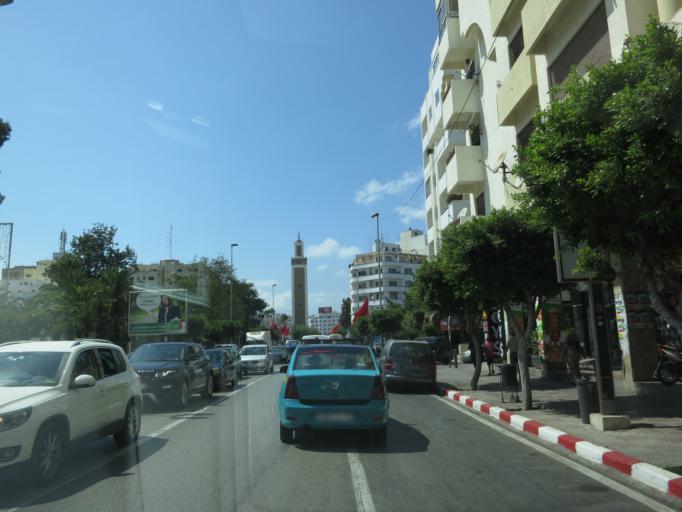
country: MA
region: Tanger-Tetouan
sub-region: Tanger-Assilah
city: Tangier
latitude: 35.7808
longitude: -5.8157
